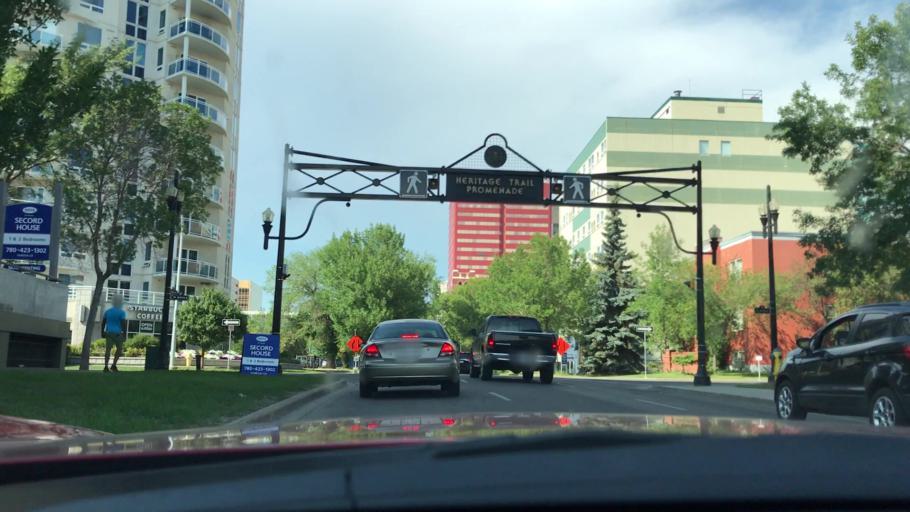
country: CA
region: Alberta
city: Edmonton
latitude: 53.5370
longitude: -113.5011
